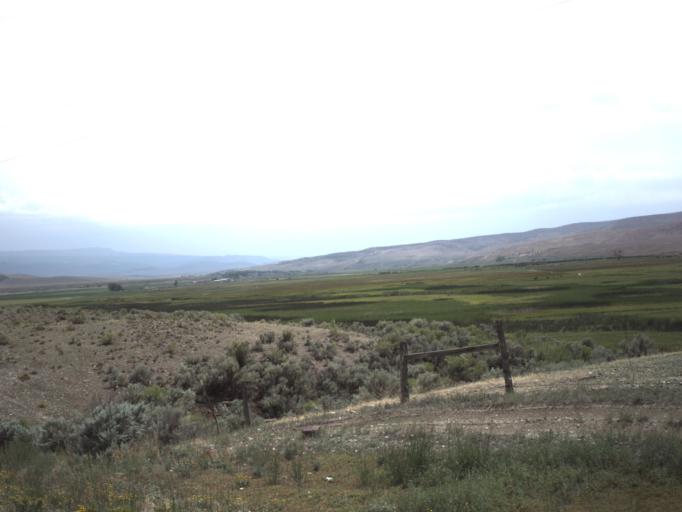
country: US
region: Utah
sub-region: Piute County
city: Junction
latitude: 38.1637
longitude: -112.0137
